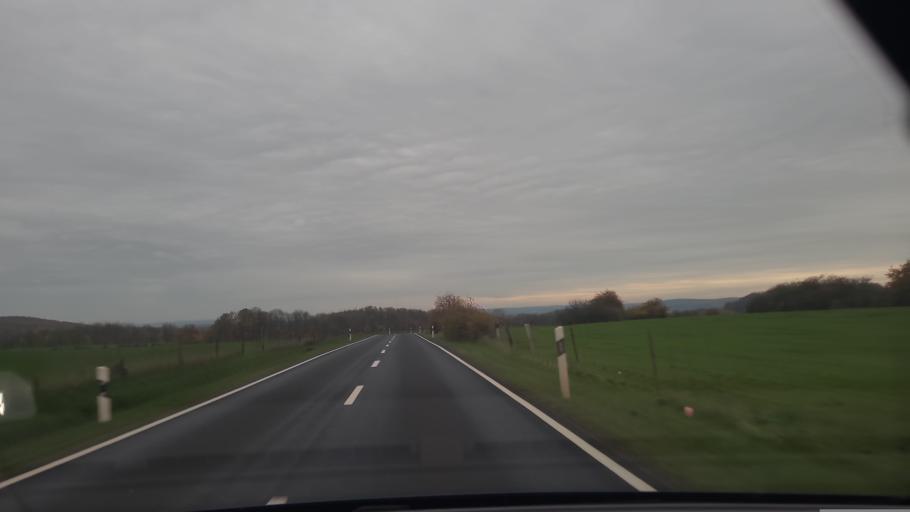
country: LU
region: Luxembourg
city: Hautcharage
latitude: 49.6021
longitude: 5.9179
